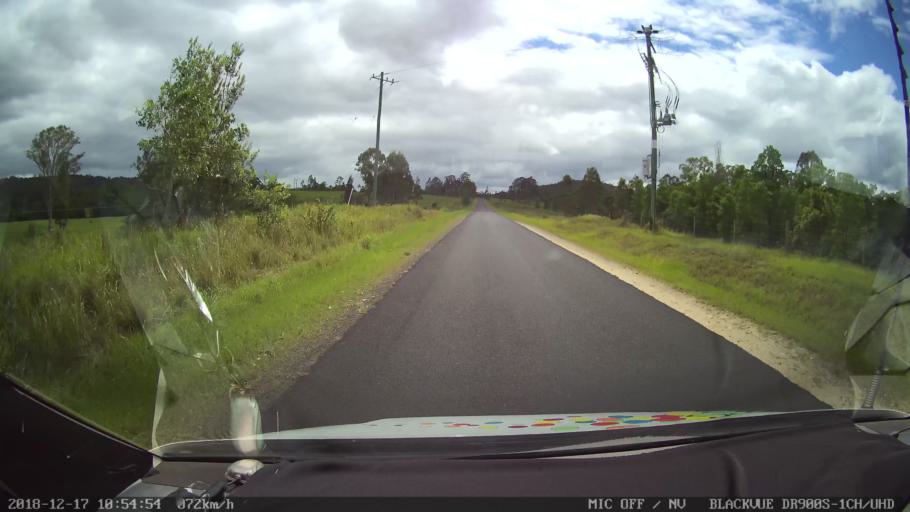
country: AU
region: New South Wales
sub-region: Tenterfield Municipality
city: Carrolls Creek
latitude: -28.8281
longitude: 152.5726
